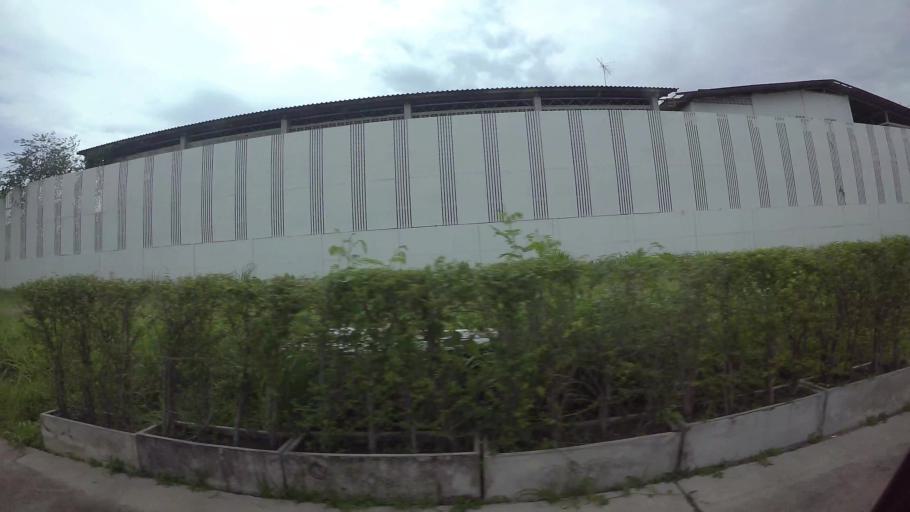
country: TH
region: Chon Buri
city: Si Racha
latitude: 13.1562
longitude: 100.9787
